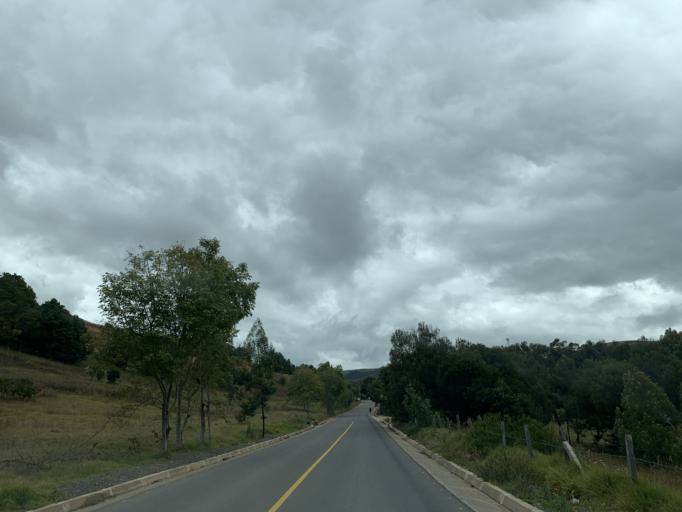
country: CO
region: Boyaca
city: Tunja
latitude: 5.5281
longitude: -73.3196
